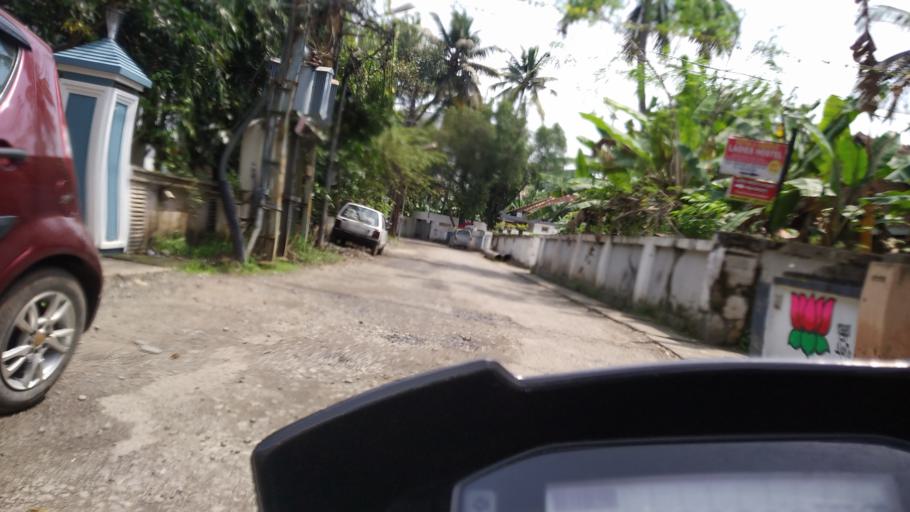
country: IN
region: Kerala
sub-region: Ernakulam
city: Cochin
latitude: 9.9591
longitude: 76.2919
